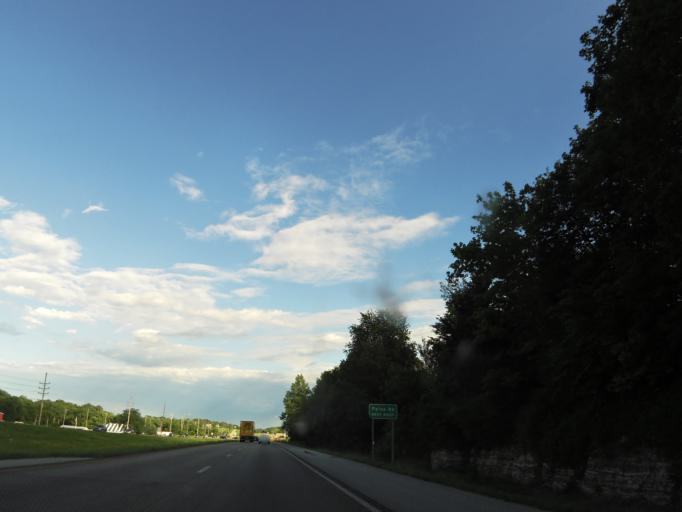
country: US
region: Missouri
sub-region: Saint Charles County
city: Wentzville
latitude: 38.8574
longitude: -90.8738
